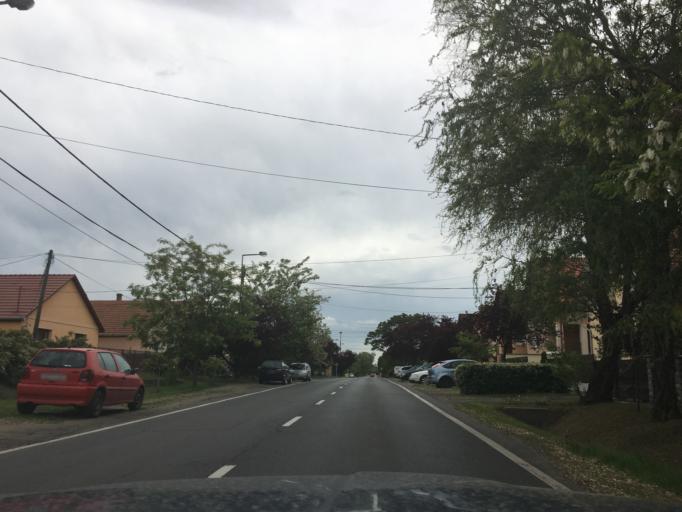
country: HU
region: Hajdu-Bihar
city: Debrecen
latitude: 47.5448
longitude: 21.6714
